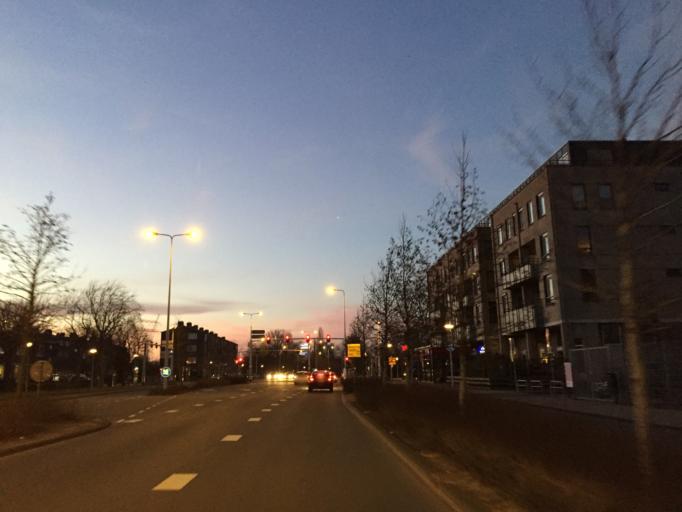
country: NL
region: South Holland
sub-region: Gemeente Leiderdorp
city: Leiderdorp
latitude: 52.1678
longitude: 4.5113
